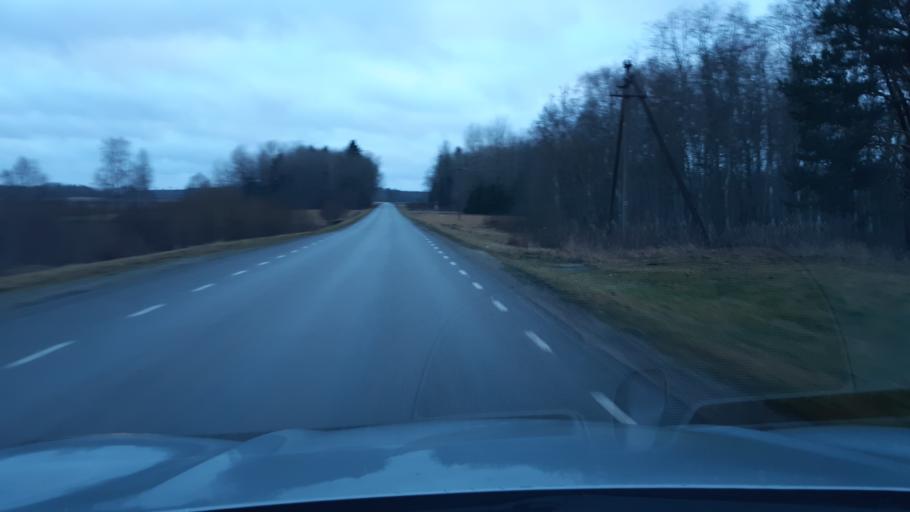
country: EE
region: Raplamaa
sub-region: Rapla vald
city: Rapla
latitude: 59.0406
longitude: 24.6770
